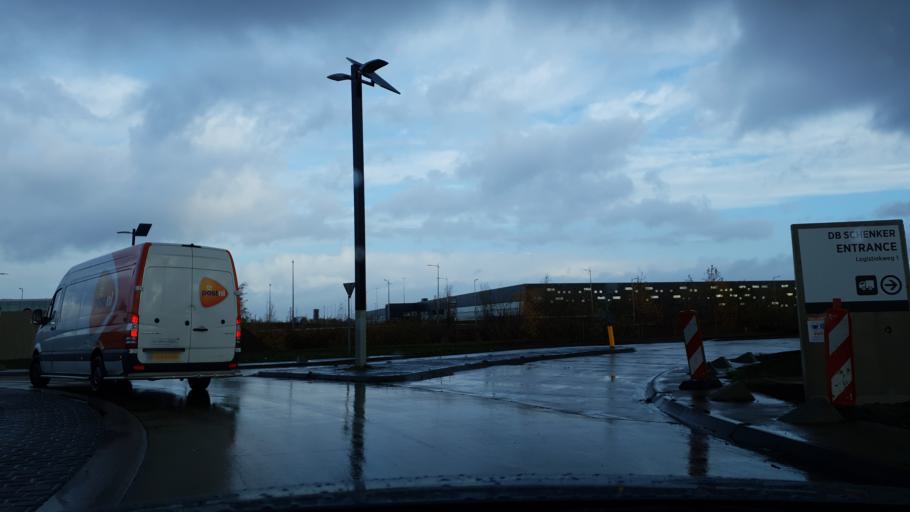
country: NL
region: Limburg
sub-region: Gemeente Peel en Maas
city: Maasbree
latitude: 51.4118
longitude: 6.0964
